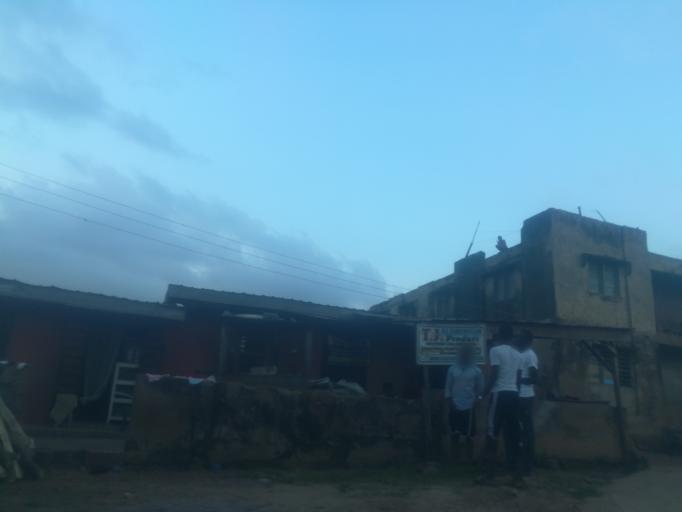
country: NG
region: Oyo
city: Ibadan
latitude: 7.4386
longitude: 3.9240
